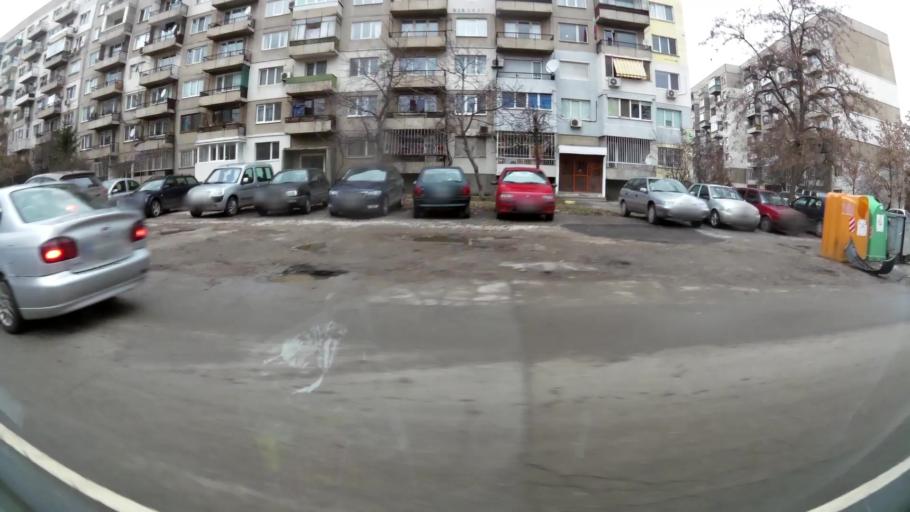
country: BG
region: Sofia-Capital
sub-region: Stolichna Obshtina
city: Sofia
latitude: 42.7287
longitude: 23.2919
